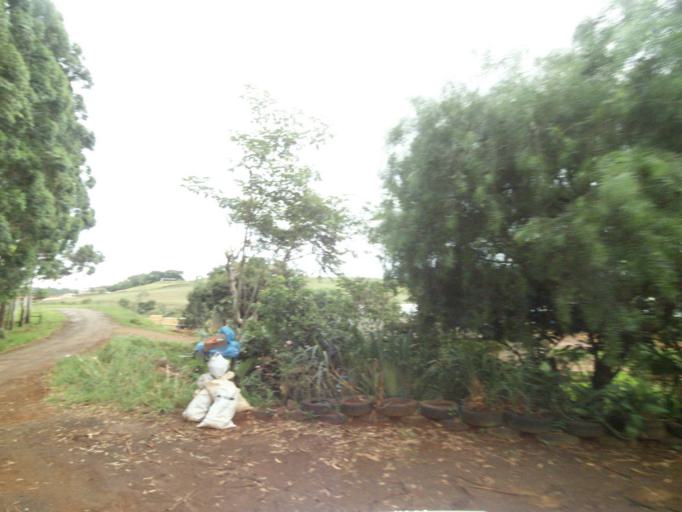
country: BR
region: Parana
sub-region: Guaraniacu
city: Guaraniacu
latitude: -25.1197
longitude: -52.8502
